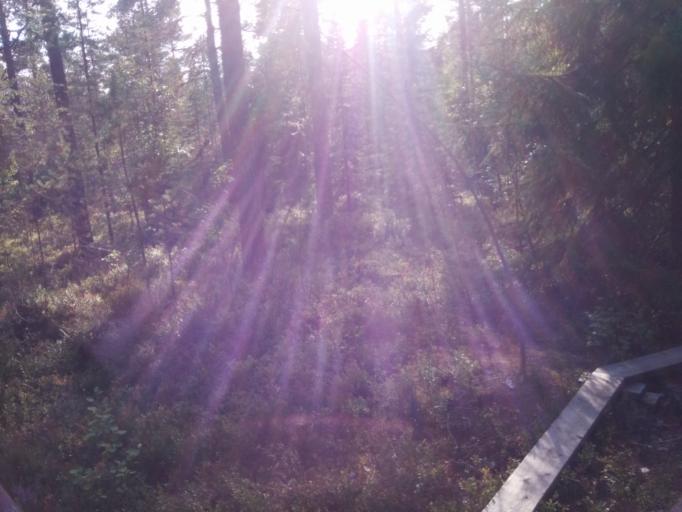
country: SE
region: Vaesterbotten
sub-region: Umea Kommun
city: Ersmark
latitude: 63.8183
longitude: 20.3614
